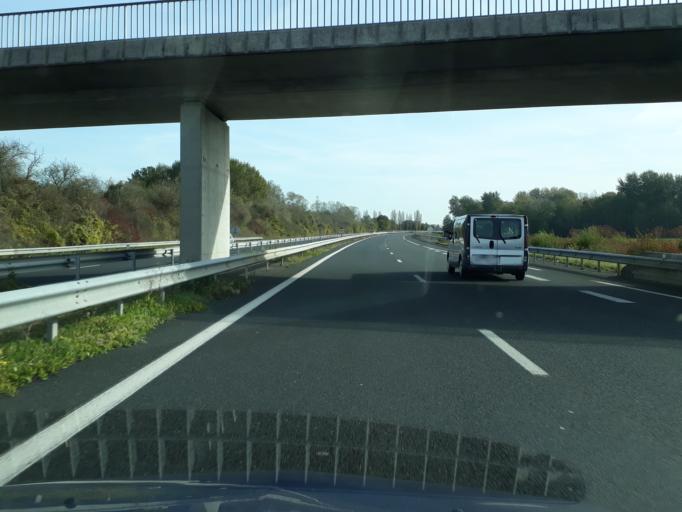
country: FR
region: Champagne-Ardenne
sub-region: Departement de l'Aube
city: Saint-Pouange
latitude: 48.2337
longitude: 4.0438
